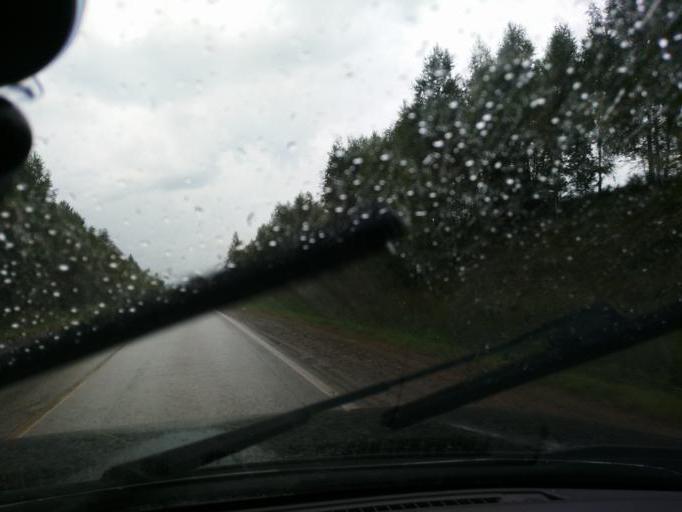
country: RU
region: Perm
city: Barda
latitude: 56.8690
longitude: 55.8905
